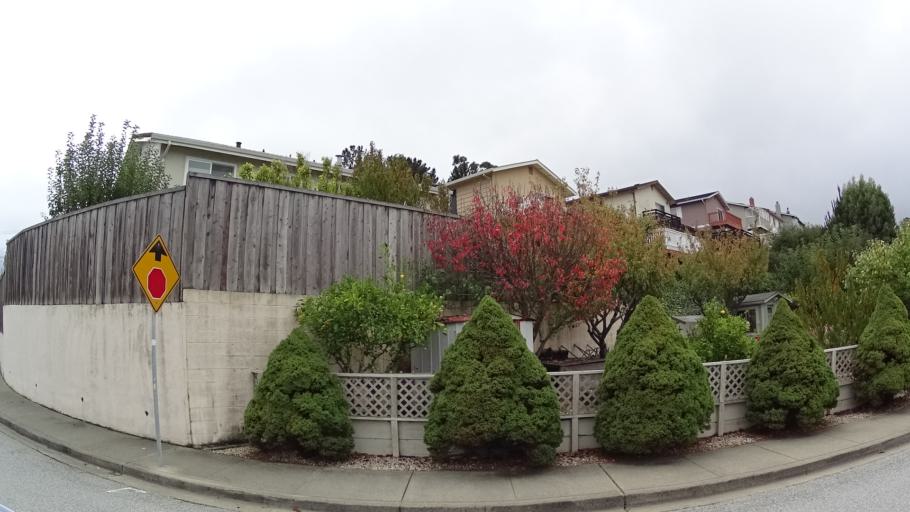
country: US
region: California
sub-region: San Mateo County
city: Millbrae
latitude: 37.5969
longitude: -122.4064
